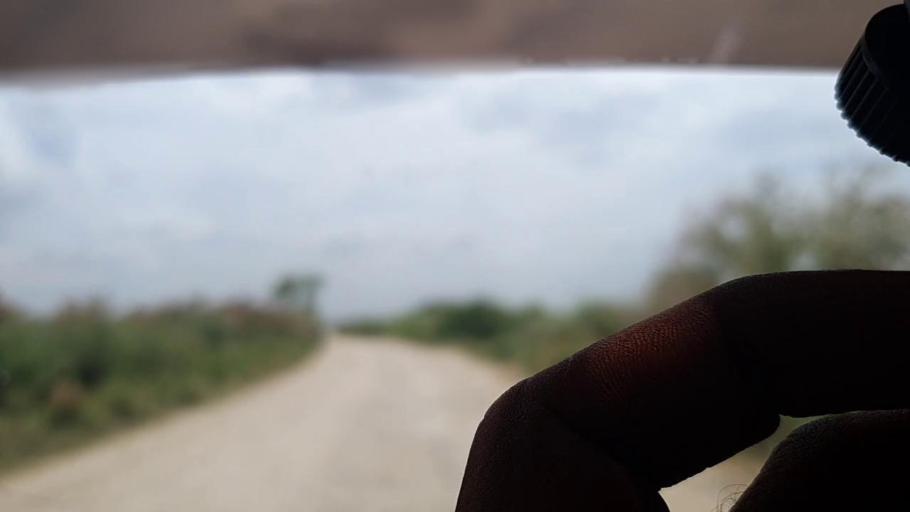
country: PK
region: Sindh
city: Rustam jo Goth
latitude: 28.0592
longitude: 68.9400
